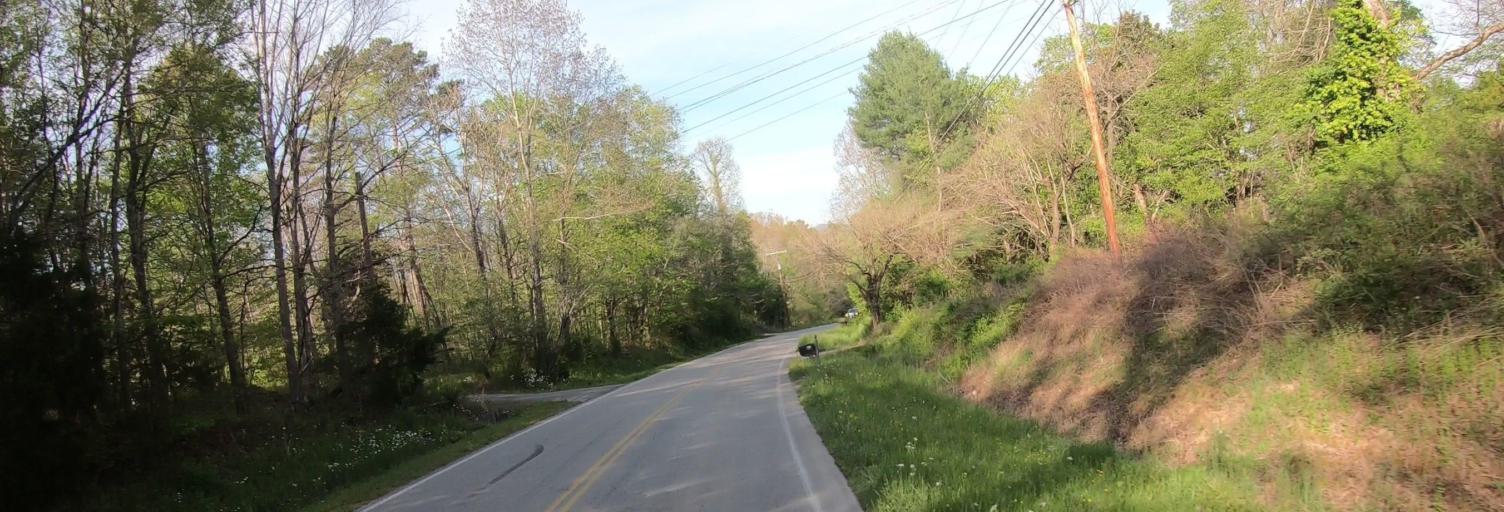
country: US
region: Tennessee
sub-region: Blount County
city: Wildwood
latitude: 35.6732
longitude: -83.7711
